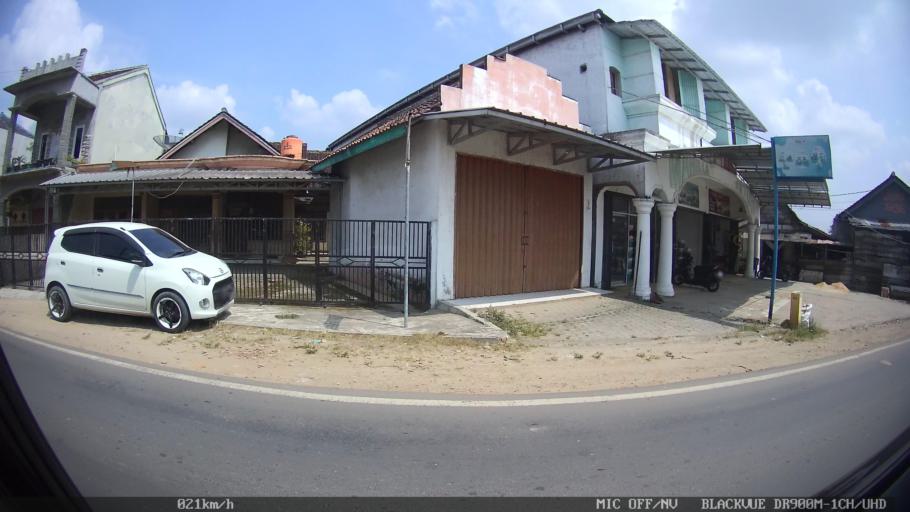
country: ID
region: Lampung
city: Pringsewu
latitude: -5.3648
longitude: 104.9730
